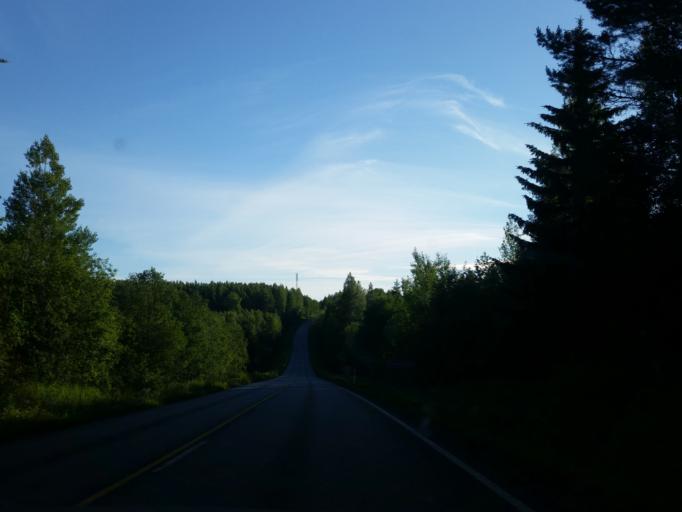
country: FI
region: Northern Savo
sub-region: Kuopio
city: Maaninka
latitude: 62.8445
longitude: 27.3536
